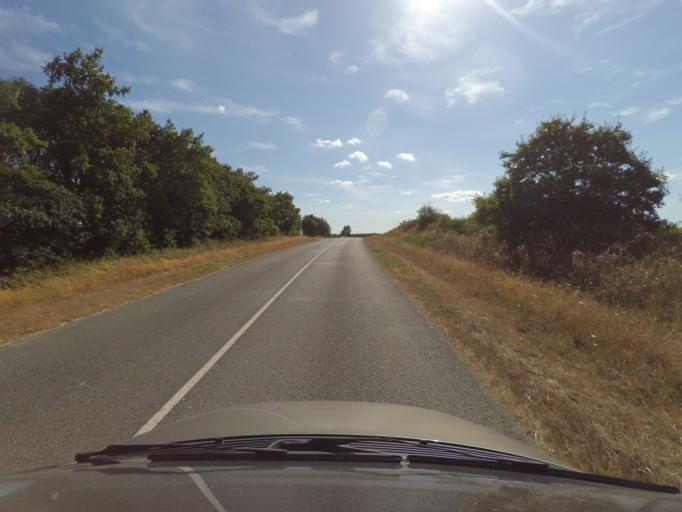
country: FR
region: Pays de la Loire
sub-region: Departement de la Loire-Atlantique
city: Le Bignon
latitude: 47.0892
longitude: -1.4545
